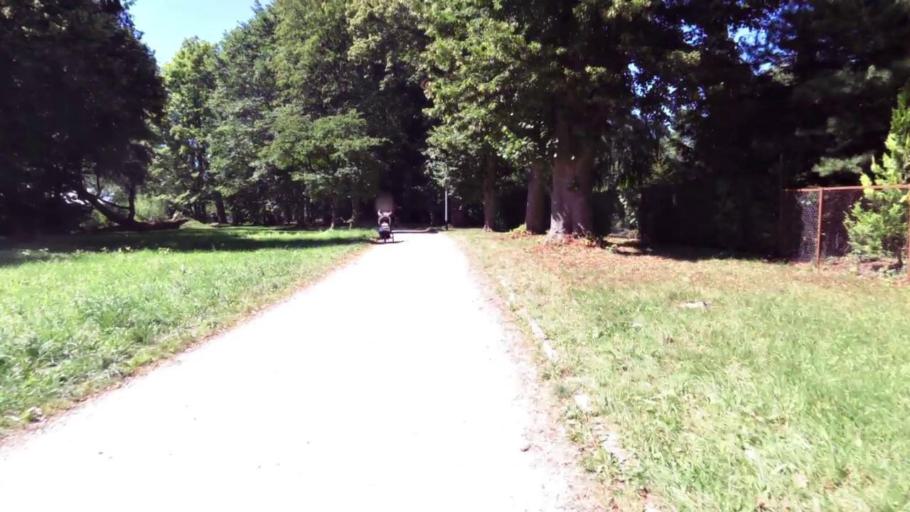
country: PL
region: West Pomeranian Voivodeship
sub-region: Powiat szczecinecki
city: Szczecinek
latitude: 53.7142
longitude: 16.6732
